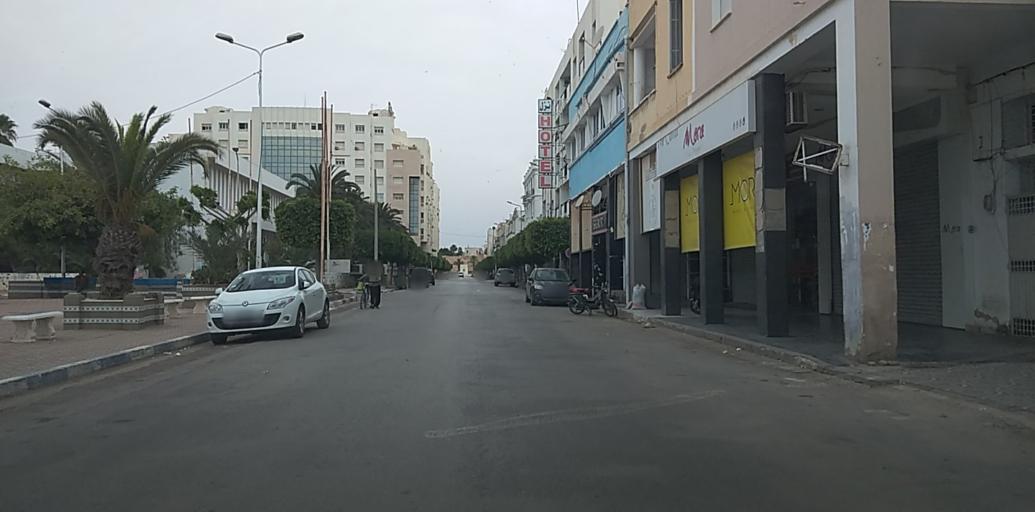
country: TN
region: Safaqis
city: Sfax
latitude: 34.7303
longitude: 10.7633
